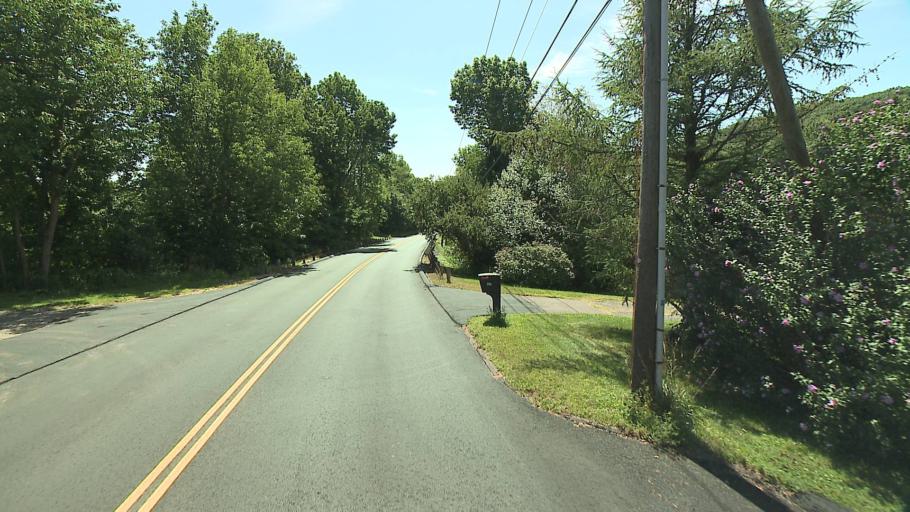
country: US
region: Connecticut
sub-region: Hartford County
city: West Simsbury
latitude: 41.9234
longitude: -72.9085
